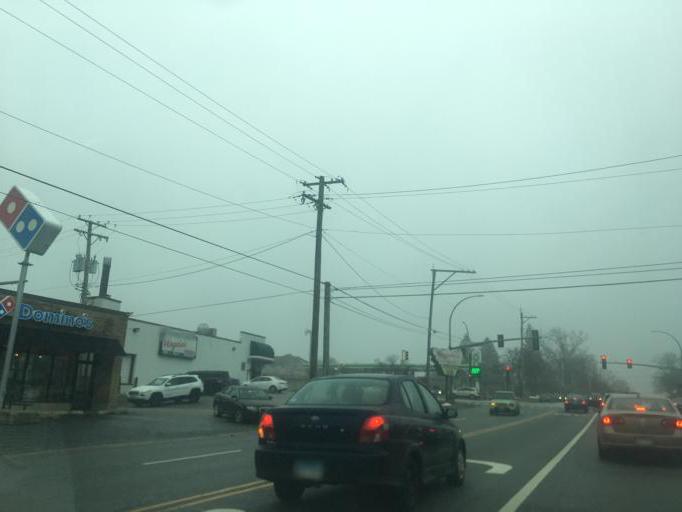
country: US
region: Illinois
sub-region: DuPage County
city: Downers Grove
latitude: 41.7855
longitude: -88.0374
